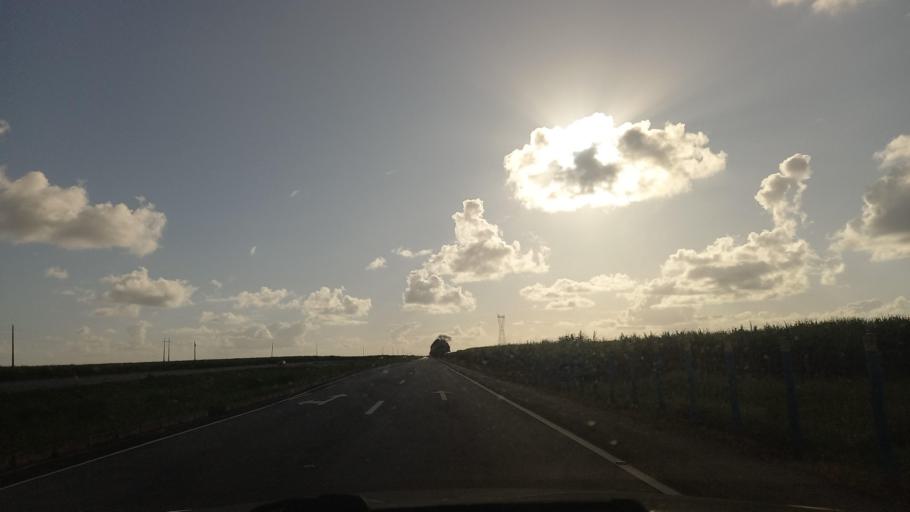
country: BR
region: Alagoas
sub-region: Sao Miguel Dos Campos
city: Sao Miguel dos Campos
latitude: -9.8041
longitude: -36.1358
